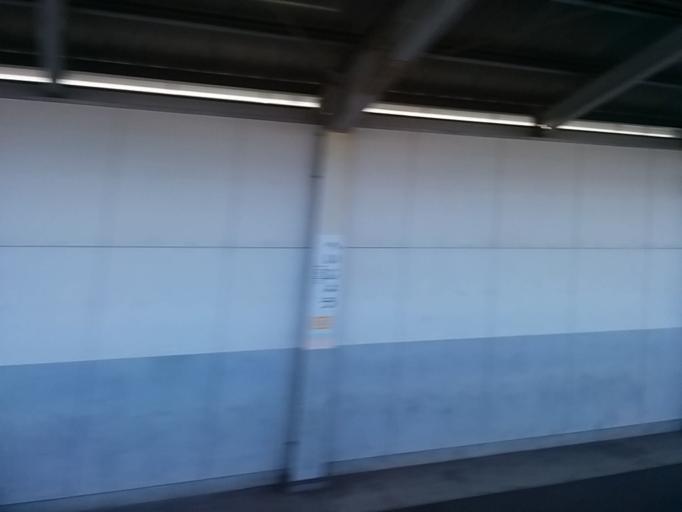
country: JP
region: Nara
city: Nara-shi
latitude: 34.7014
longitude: 135.7846
